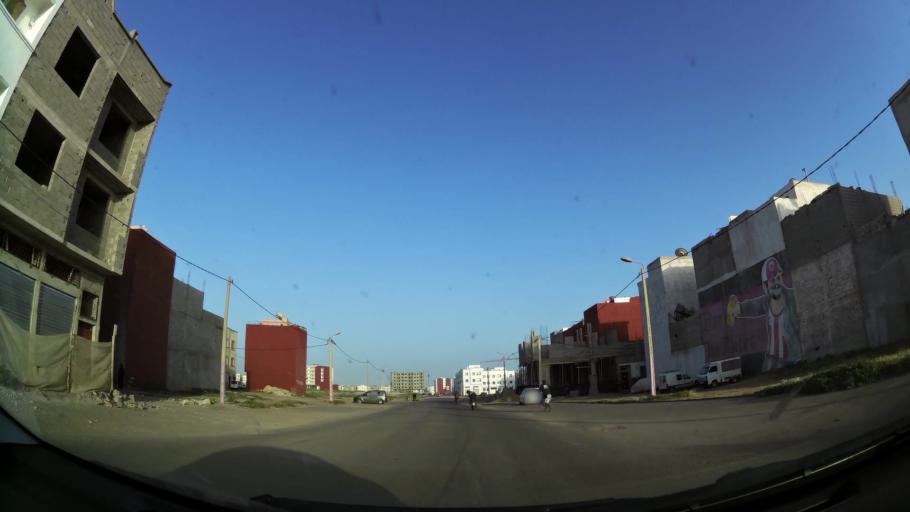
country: MA
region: Oued ed Dahab-Lagouira
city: Dakhla
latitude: 30.4014
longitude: -9.5690
